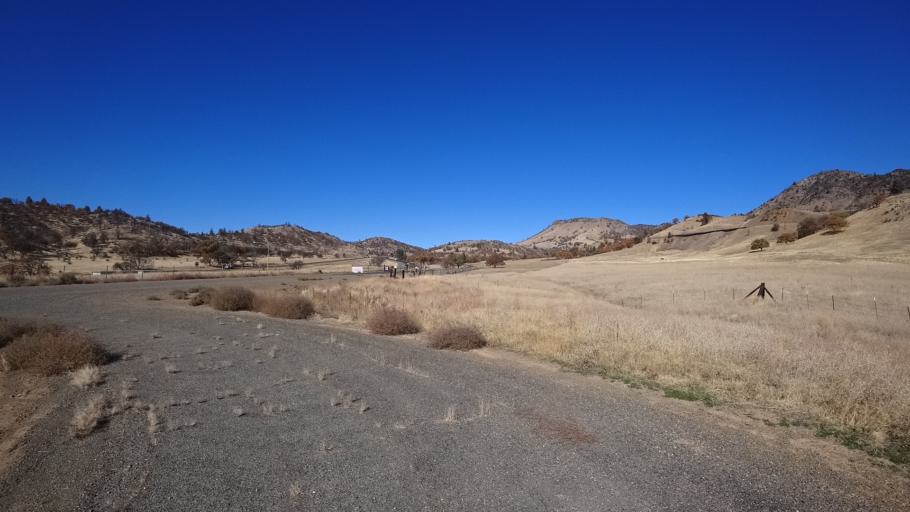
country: US
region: California
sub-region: Siskiyou County
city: Yreka
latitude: 41.9589
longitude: -122.5936
